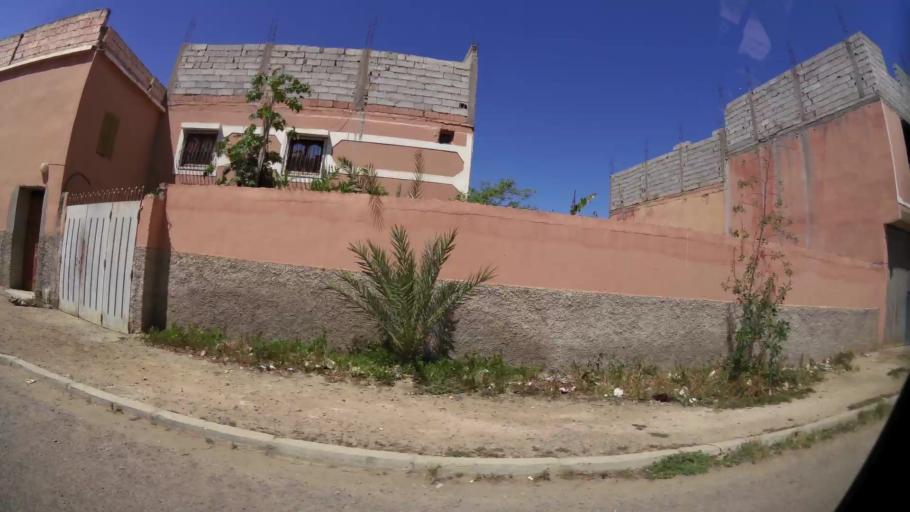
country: MA
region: Souss-Massa-Draa
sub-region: Inezgane-Ait Mellou
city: Inezgane
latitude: 30.3191
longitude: -9.5040
